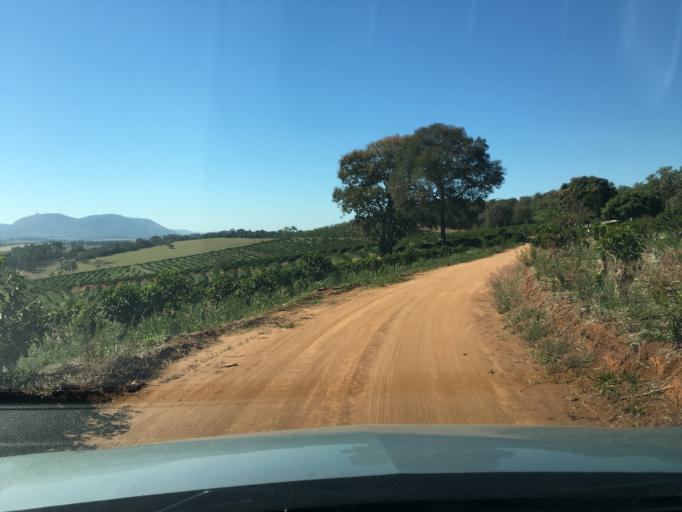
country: BR
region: Minas Gerais
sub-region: Campestre
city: Campestre
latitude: -21.5904
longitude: -46.2071
